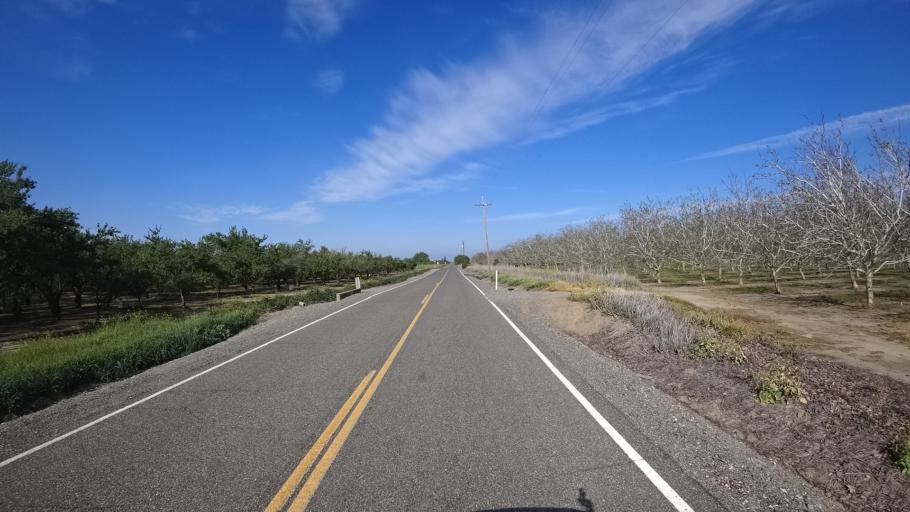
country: US
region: California
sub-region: Glenn County
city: Hamilton City
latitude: 39.6307
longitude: -122.0350
